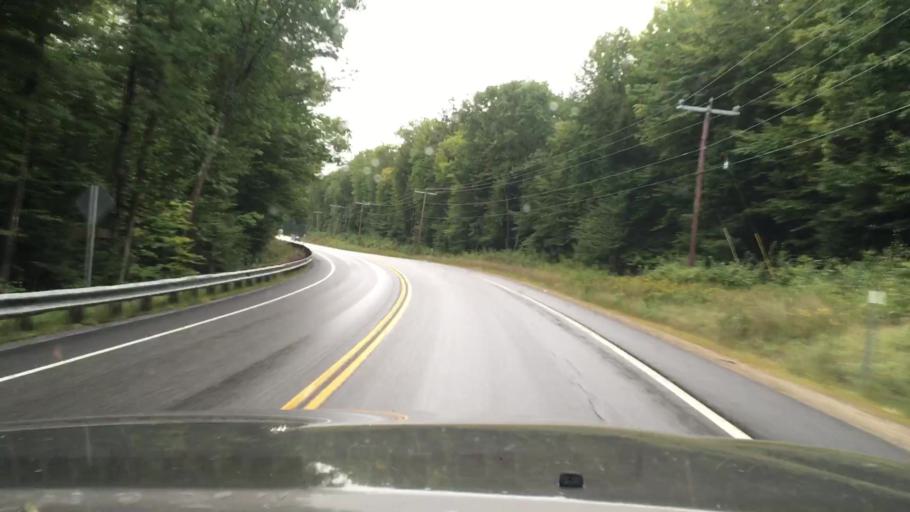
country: US
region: New Hampshire
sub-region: Hillsborough County
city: Antrim
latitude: 43.0891
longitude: -71.9674
